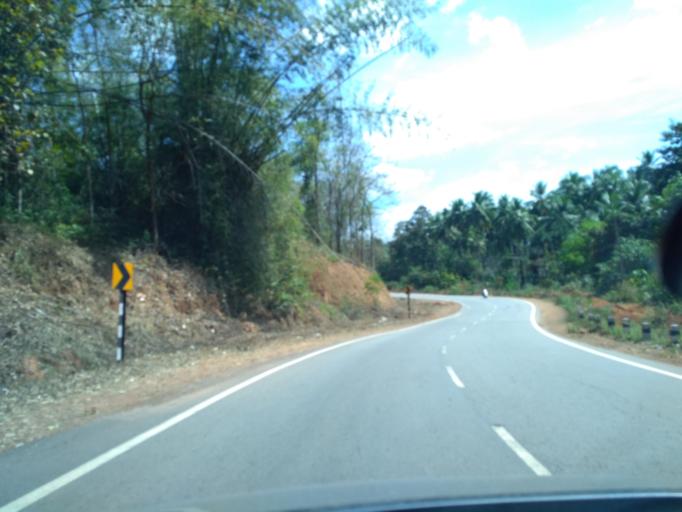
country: IN
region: Karnataka
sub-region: Dakshina Kannada
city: Sulya
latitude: 12.5197
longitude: 75.4789
